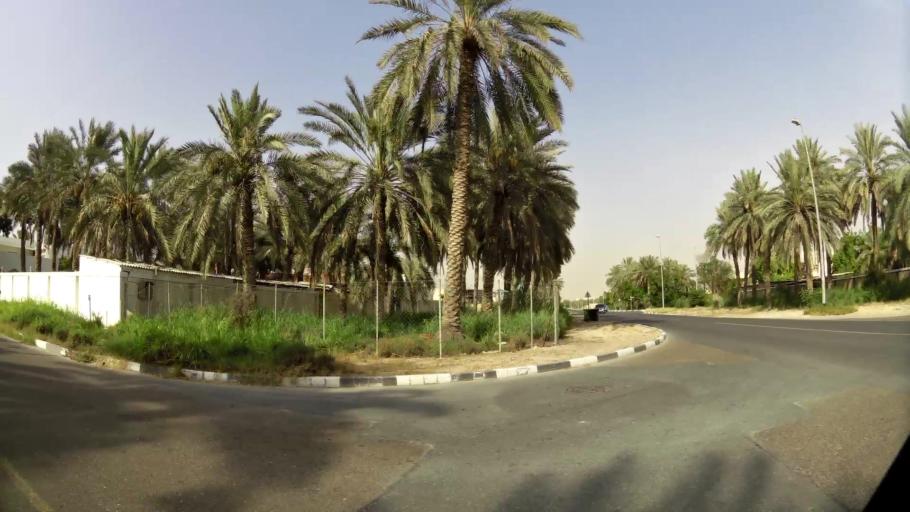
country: AE
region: Ash Shariqah
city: Sharjah
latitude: 25.2503
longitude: 55.4198
